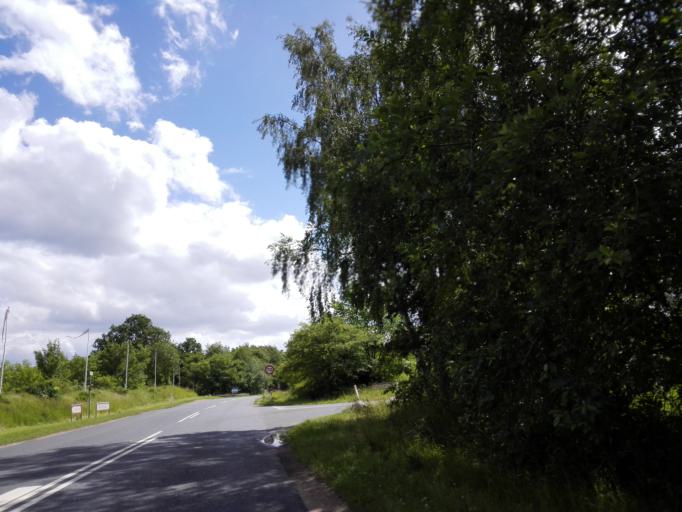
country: DK
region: Capital Region
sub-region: Allerod Kommune
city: Lynge
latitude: 55.8246
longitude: 12.3024
